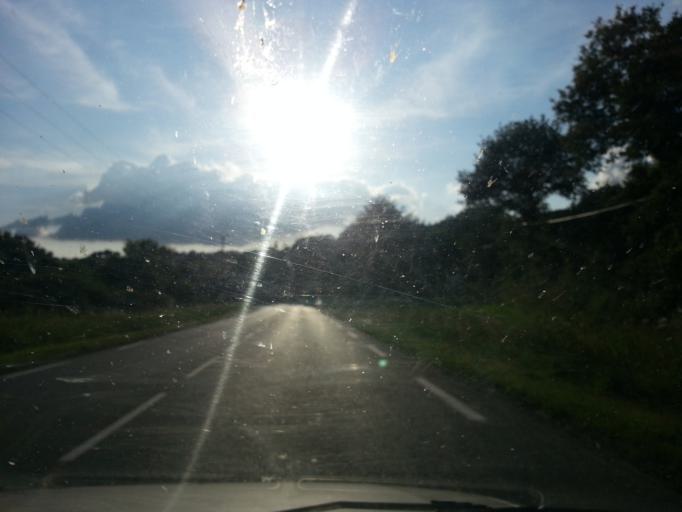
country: FR
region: Brittany
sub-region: Departement du Finistere
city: Carhaix-Plouguer
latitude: 48.2703
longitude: -3.5946
